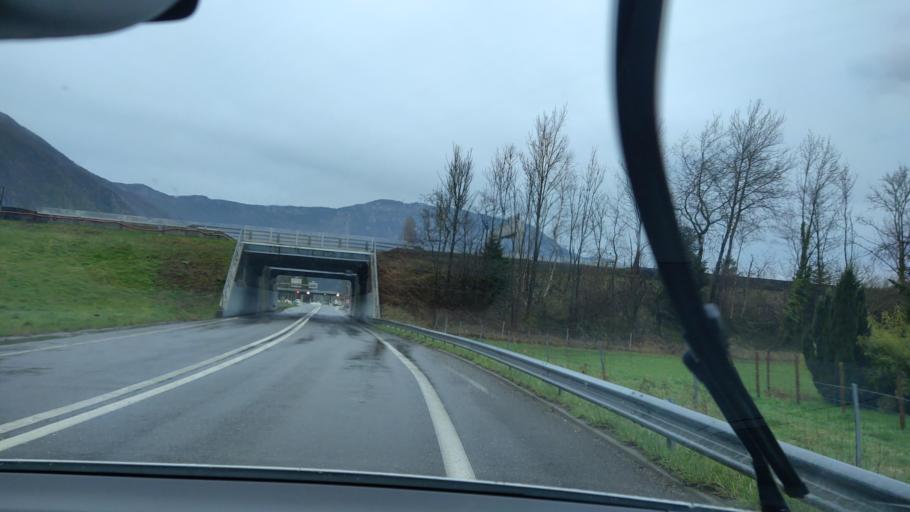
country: FR
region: Rhone-Alpes
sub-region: Departement de la Savoie
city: Novalaise
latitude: 45.5796
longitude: 5.7977
